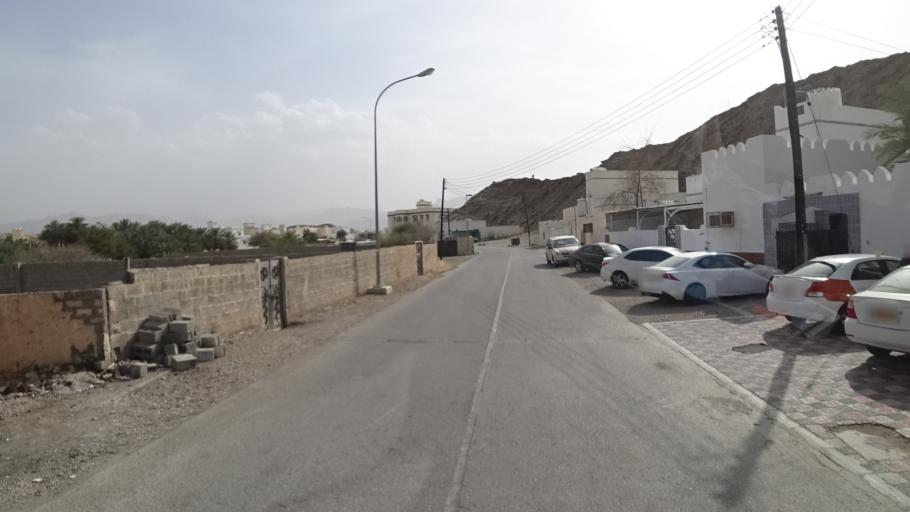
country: OM
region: Muhafazat Masqat
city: Bawshar
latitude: 23.3900
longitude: 58.5181
